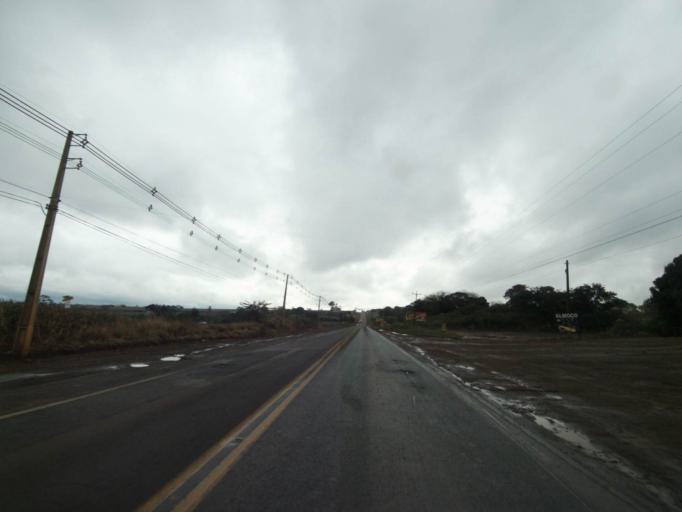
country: BR
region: Parana
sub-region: Marechal Candido Rondon
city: Marechal Candido Rondon
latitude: -24.5686
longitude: -54.0167
